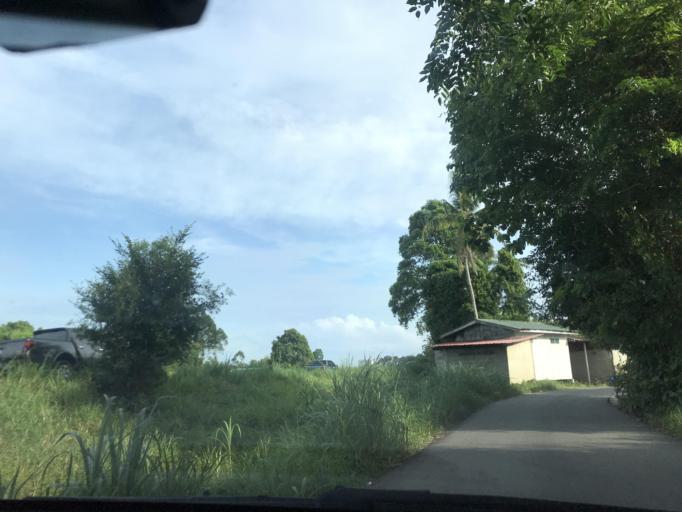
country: MY
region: Kelantan
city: Kota Bharu
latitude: 6.1356
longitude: 102.2240
